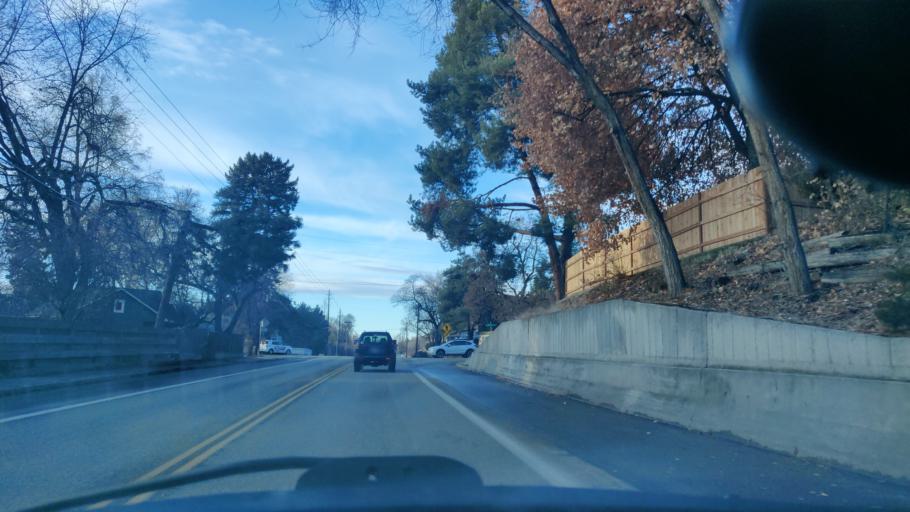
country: US
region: Idaho
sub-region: Ada County
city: Boise
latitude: 43.6430
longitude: -116.2137
